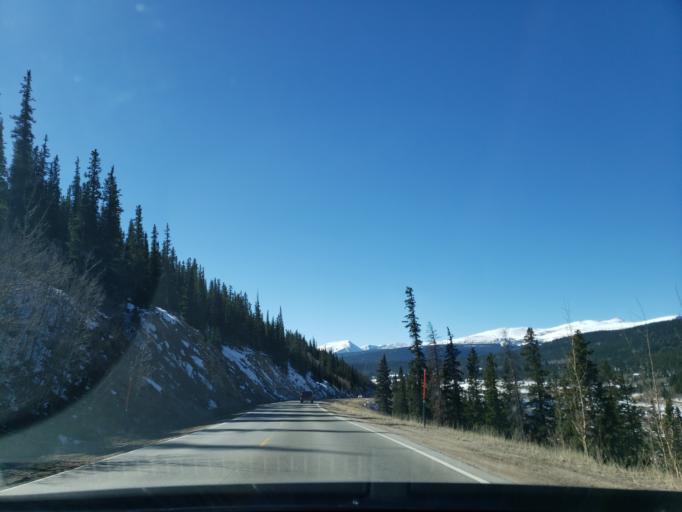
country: US
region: Colorado
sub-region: Park County
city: Fairplay
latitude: 39.3218
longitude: -106.0541
